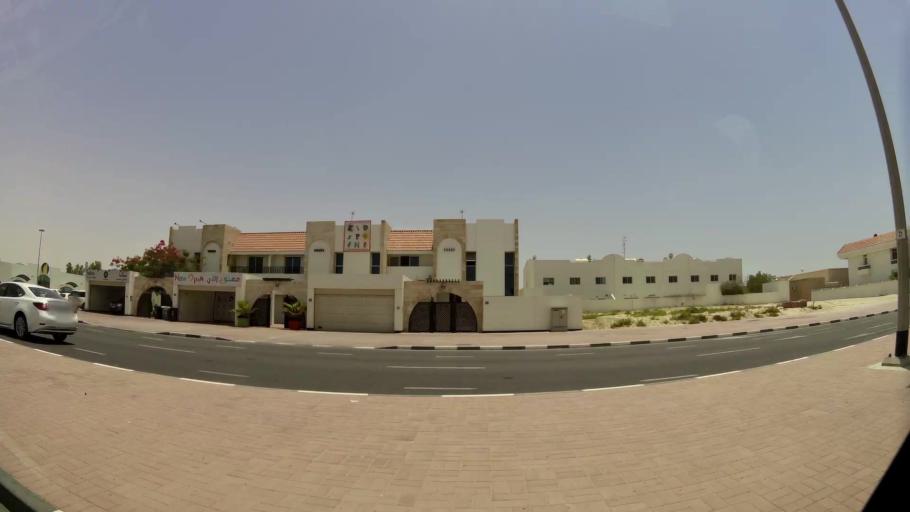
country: AE
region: Dubai
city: Dubai
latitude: 25.1703
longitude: 55.2268
